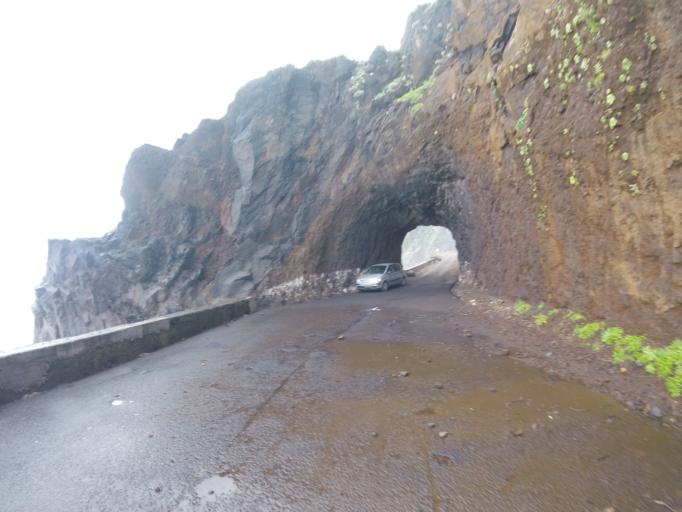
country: PT
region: Madeira
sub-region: Porto Moniz
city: Porto Moniz
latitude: 32.8524
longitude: -17.1501
